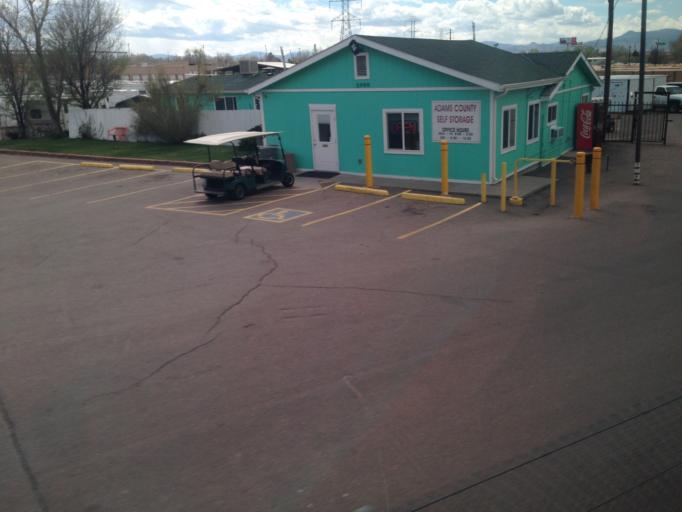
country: US
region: Colorado
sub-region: Adams County
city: Berkley
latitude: 39.8060
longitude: -105.0072
